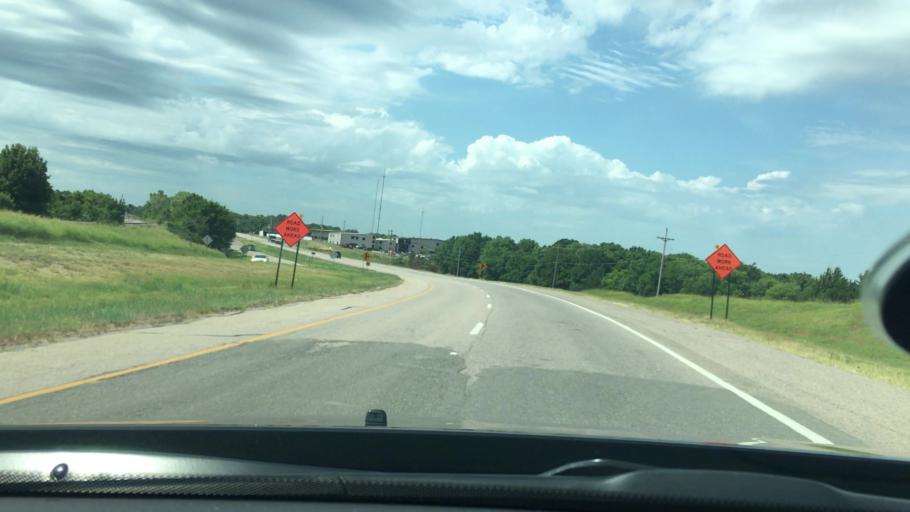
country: US
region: Oklahoma
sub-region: Pontotoc County
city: Ada
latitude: 34.7418
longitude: -96.7087
